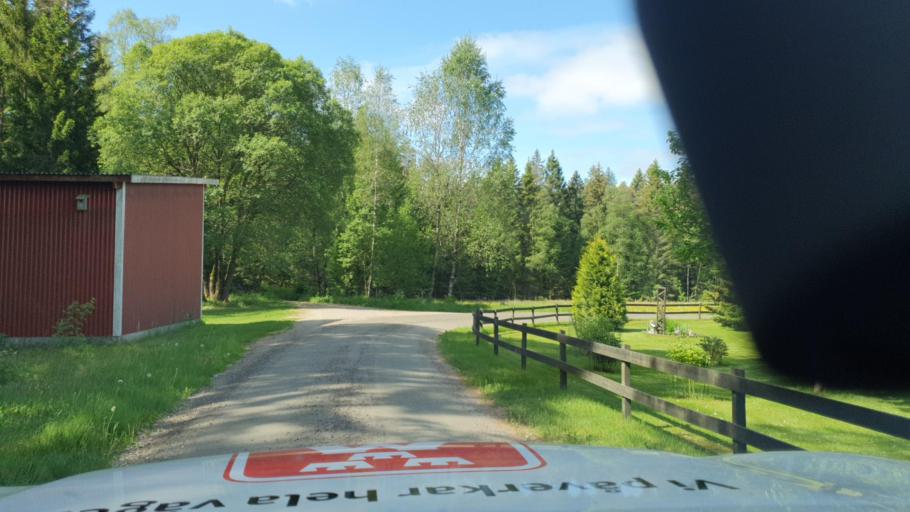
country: SE
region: Vaestra Goetaland
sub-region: Herrljunga Kommun
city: Herrljunga
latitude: 57.9402
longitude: 13.0075
